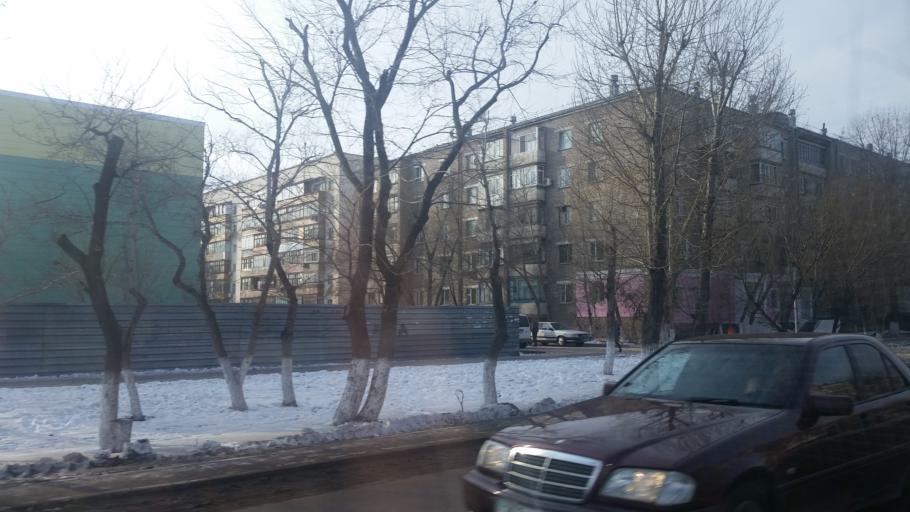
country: KZ
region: Astana Qalasy
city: Astana
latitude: 51.1979
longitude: 71.3950
